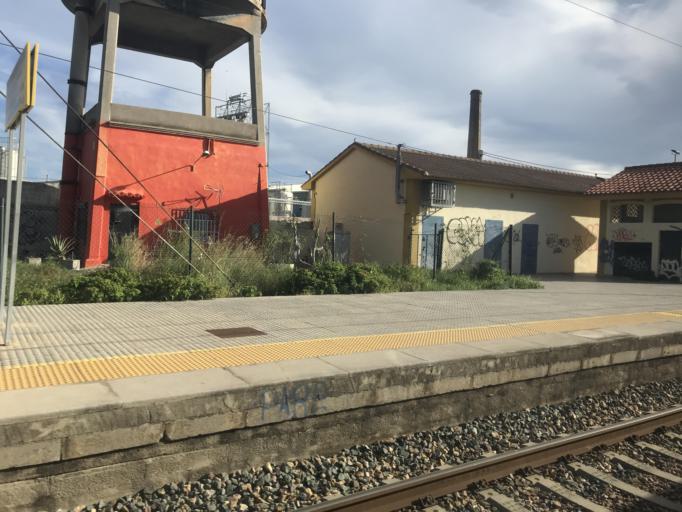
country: ES
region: Valencia
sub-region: Provincia de Castello
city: Benicarlo
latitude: 40.4282
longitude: 0.4154
